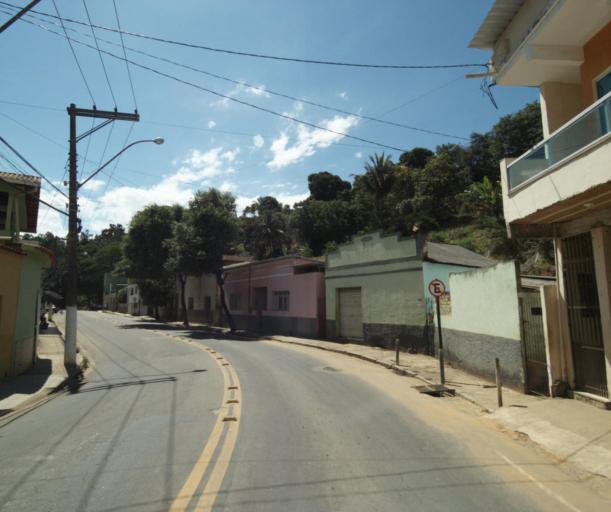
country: BR
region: Espirito Santo
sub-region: Mimoso Do Sul
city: Mimoso do Sul
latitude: -21.0673
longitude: -41.3580
